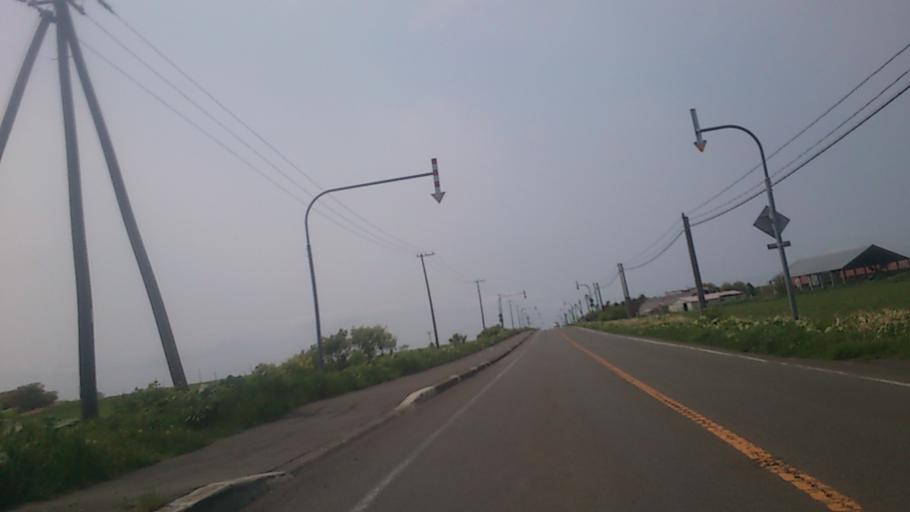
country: JP
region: Hokkaido
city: Nemuro
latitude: 43.2722
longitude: 145.5343
